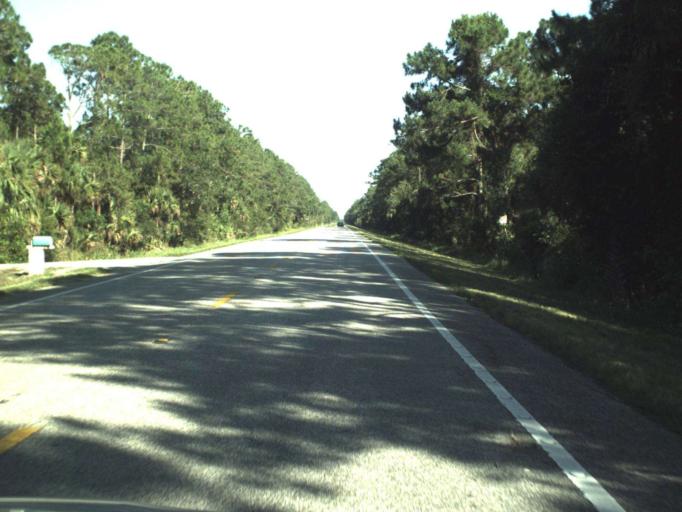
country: US
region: Florida
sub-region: Seminole County
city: Geneva
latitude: 28.6920
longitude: -80.9985
